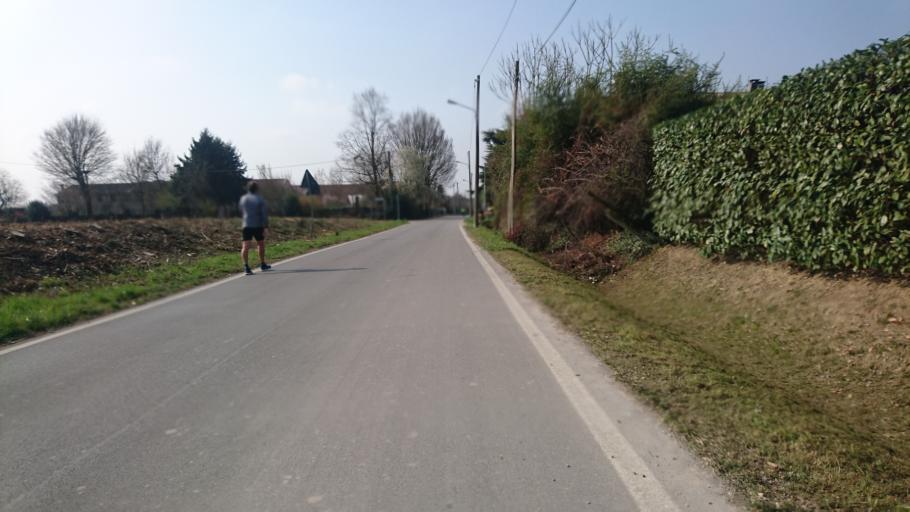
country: IT
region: Veneto
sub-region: Provincia di Padova
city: Mandriola-Sant'Agostino
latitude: 45.3789
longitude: 11.8305
